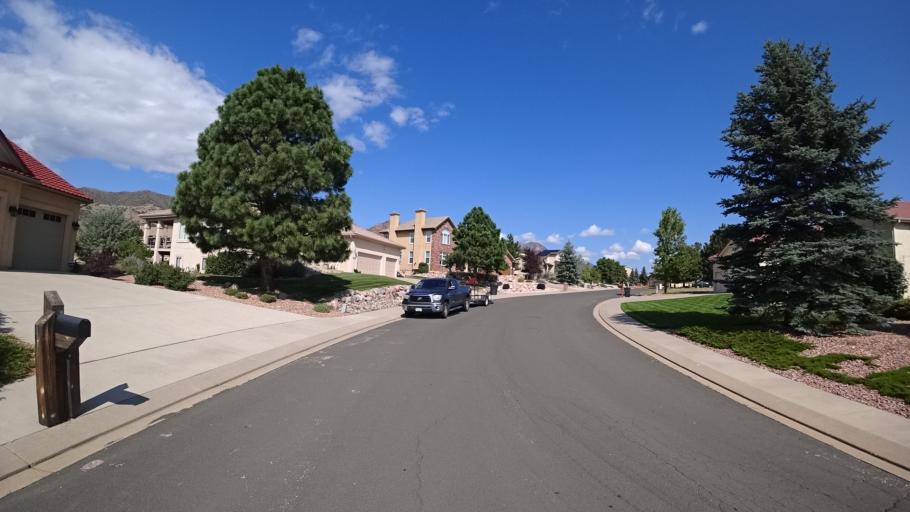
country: US
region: Colorado
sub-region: El Paso County
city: Manitou Springs
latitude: 38.9121
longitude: -104.8707
